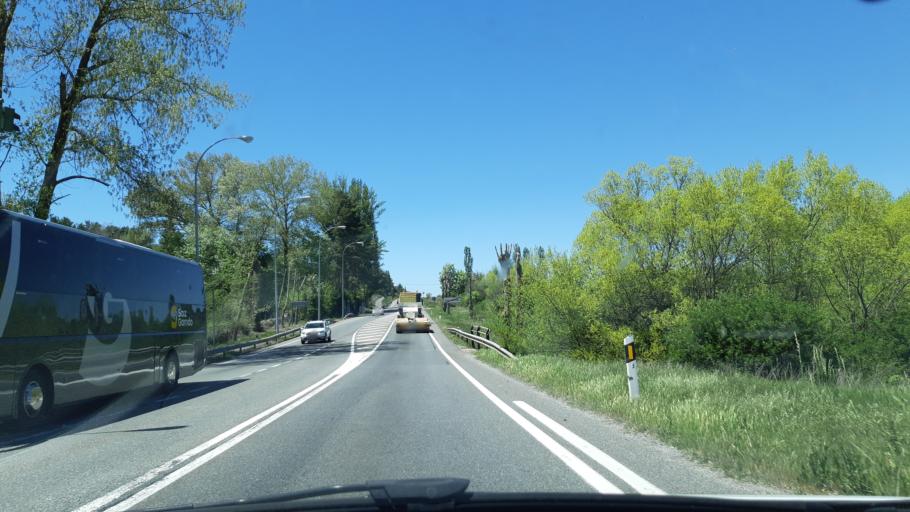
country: ES
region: Castille and Leon
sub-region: Provincia de Avila
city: Peguerinos
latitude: 40.7158
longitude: -4.1990
